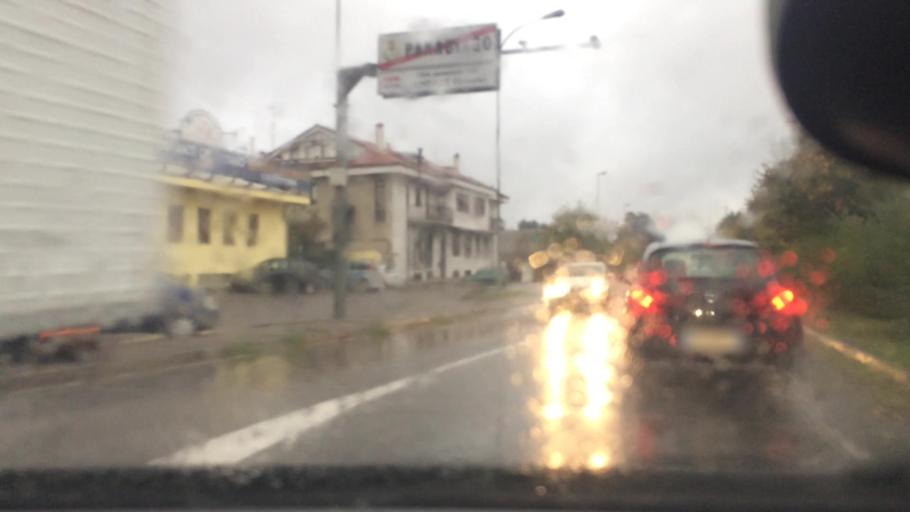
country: IT
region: Lombardy
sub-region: Citta metropolitana di Milano
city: Parabiago
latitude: 45.5490
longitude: 8.9587
